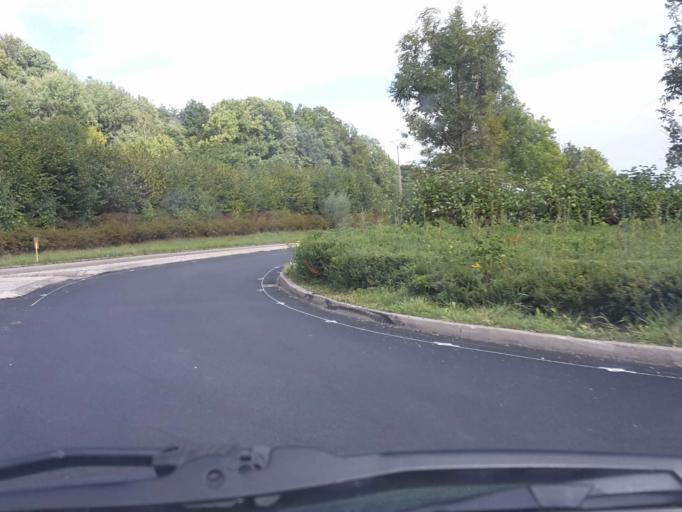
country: FR
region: Franche-Comte
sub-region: Departement du Doubs
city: Montfaucon
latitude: 47.2346
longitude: 6.0947
